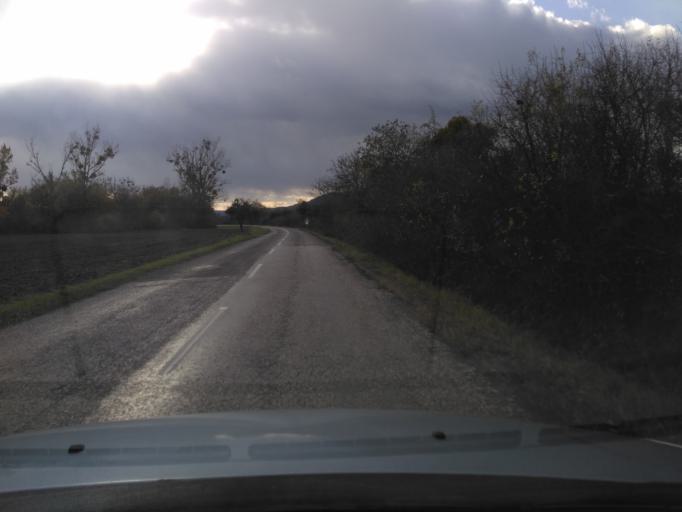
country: HU
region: Borsod-Abauj-Zemplen
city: Satoraljaujhely
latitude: 48.4116
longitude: 21.7125
